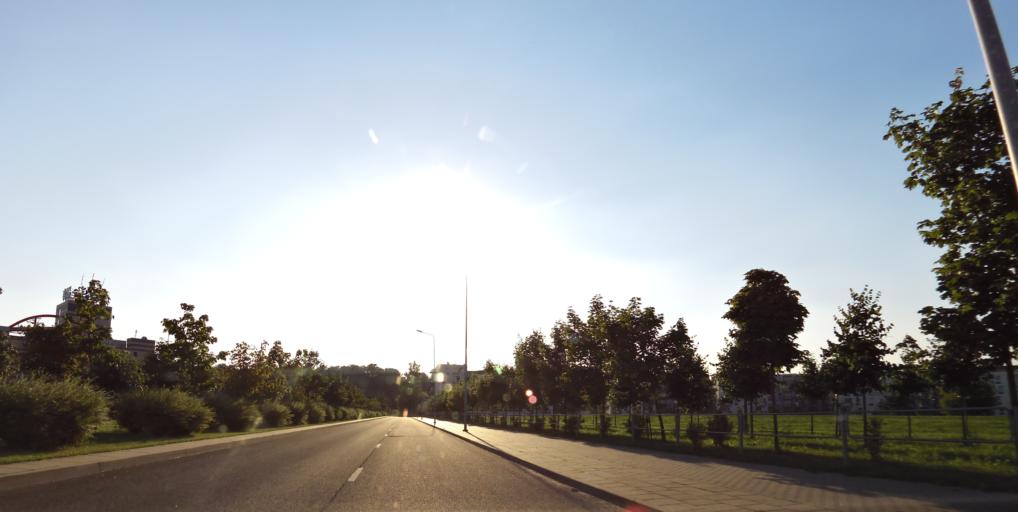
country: LT
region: Vilnius County
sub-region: Vilnius
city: Vilnius
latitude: 54.7174
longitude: 25.2790
